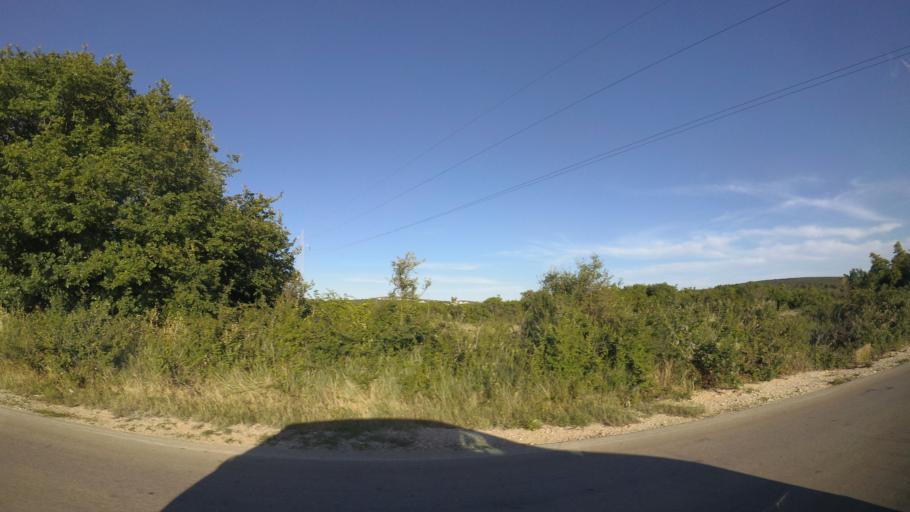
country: HR
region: Zadarska
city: Sukosan
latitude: 44.0577
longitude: 15.3337
